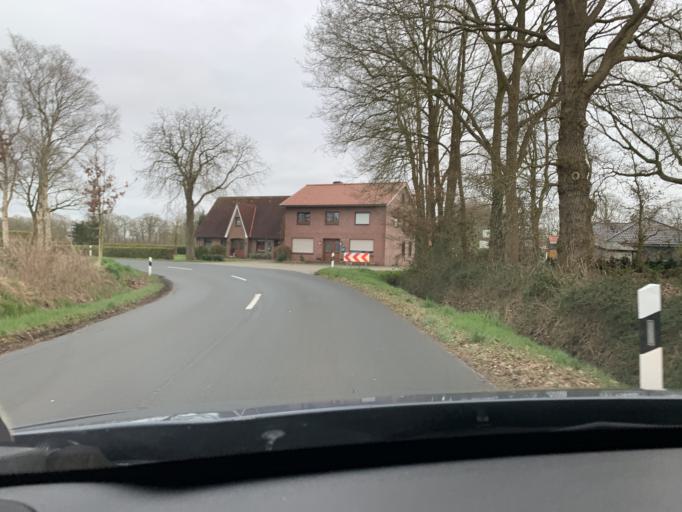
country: DE
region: Lower Saxony
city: Detern
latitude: 53.2542
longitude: 7.7162
